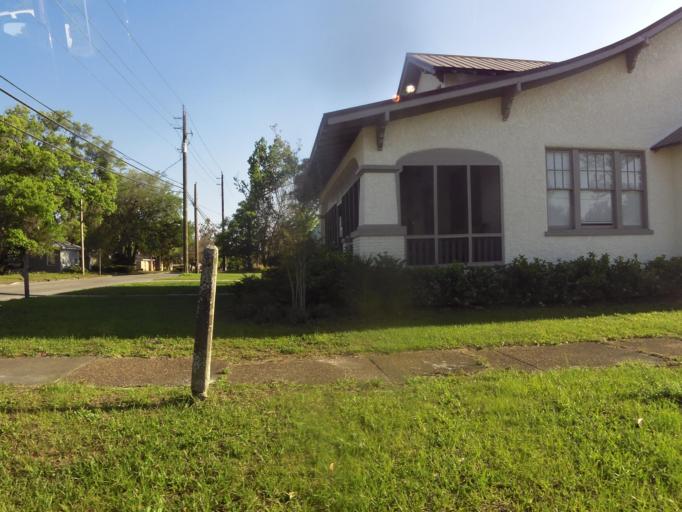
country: US
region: Florida
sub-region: Putnam County
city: Palatka
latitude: 29.6453
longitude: -81.6499
